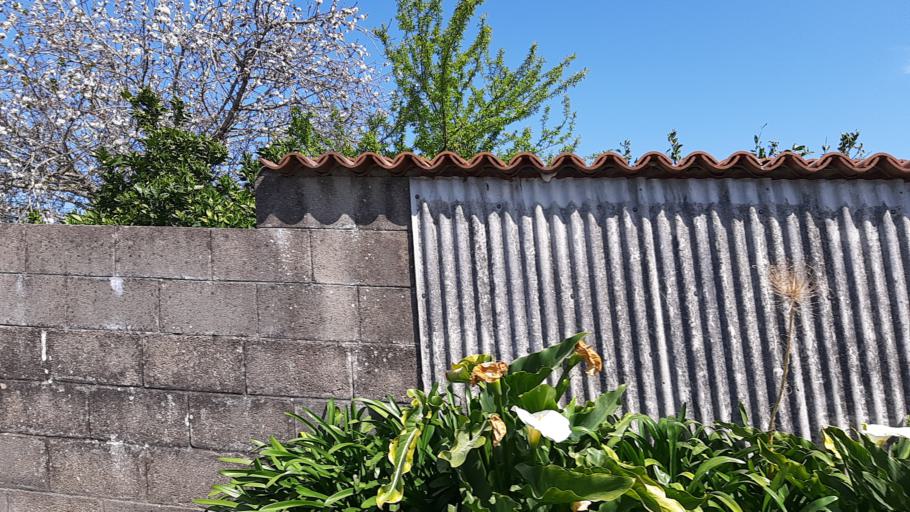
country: ES
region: Galicia
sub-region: Provincia de Pontevedra
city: O Rosal
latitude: 41.9284
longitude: -8.8466
